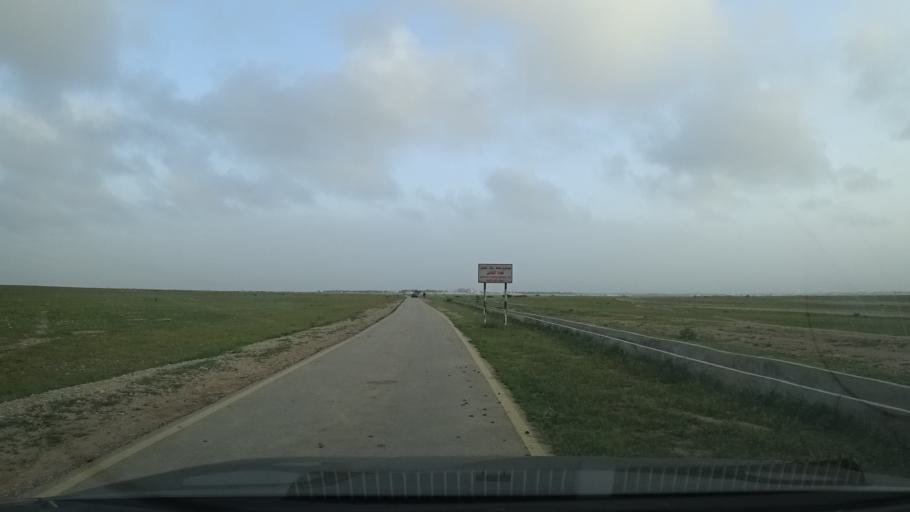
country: OM
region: Zufar
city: Salalah
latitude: 17.0814
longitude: 54.2317
